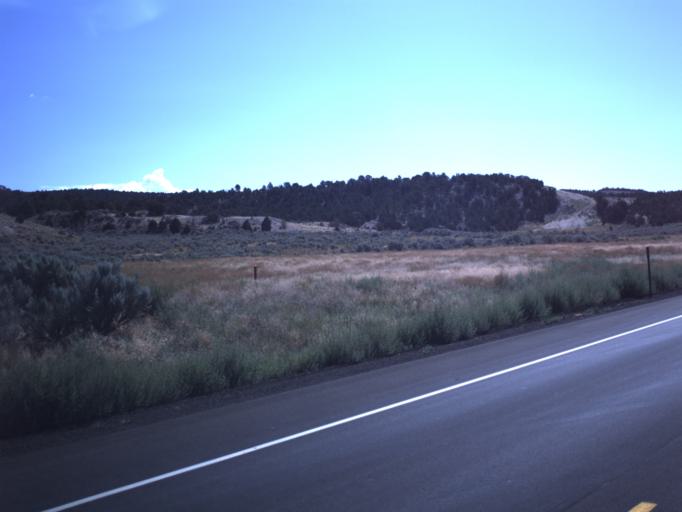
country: US
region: Utah
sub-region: Utah County
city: Eagle Mountain
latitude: 39.9896
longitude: -112.2667
